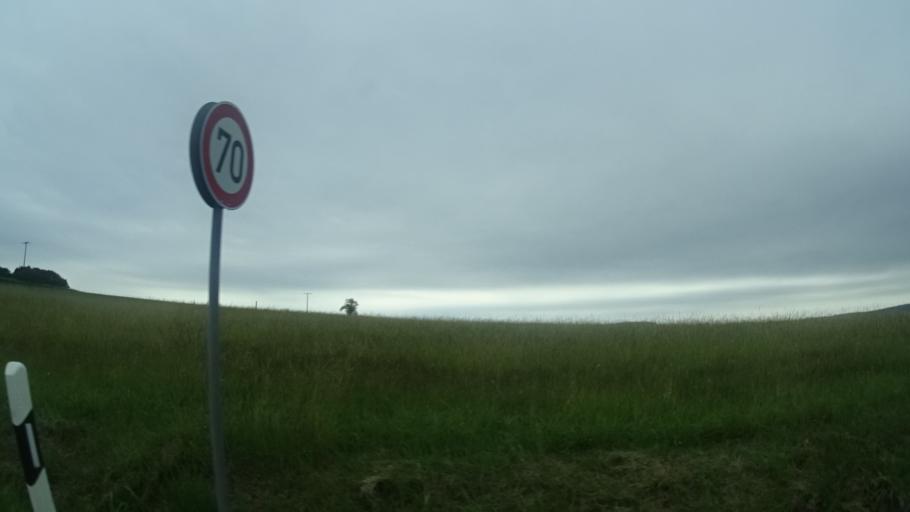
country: DE
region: Bavaria
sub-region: Regierungsbezirk Unterfranken
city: Krombach
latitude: 50.0855
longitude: 9.2218
